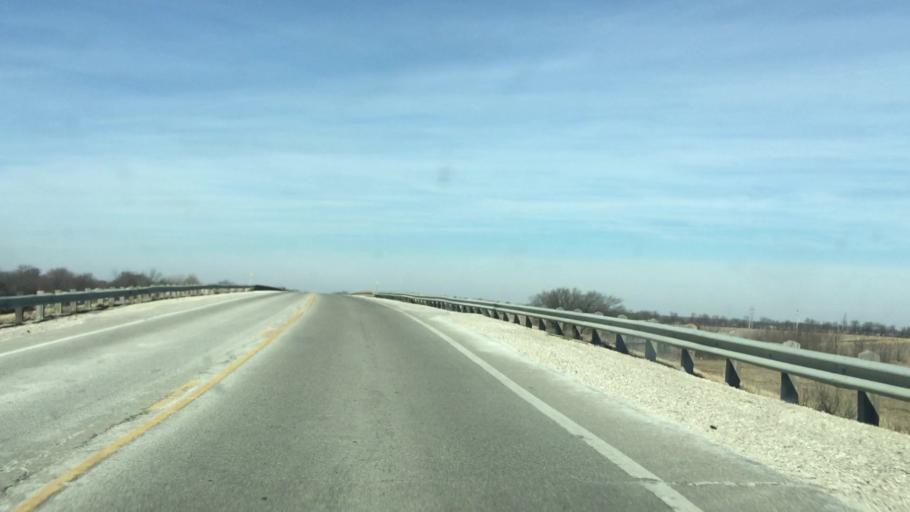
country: US
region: Kansas
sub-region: Labette County
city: Parsons
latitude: 37.3816
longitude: -95.2599
